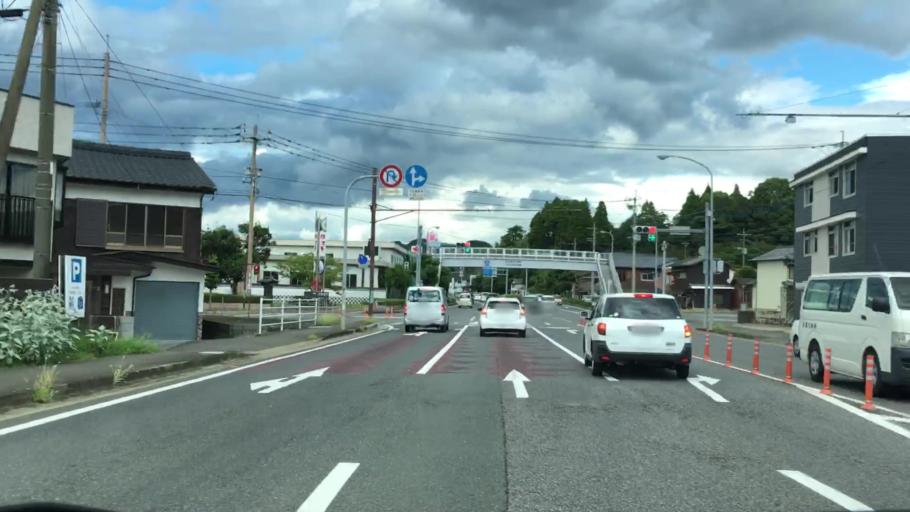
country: JP
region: Saga Prefecture
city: Imaricho-ko
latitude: 33.2726
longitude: 129.8899
